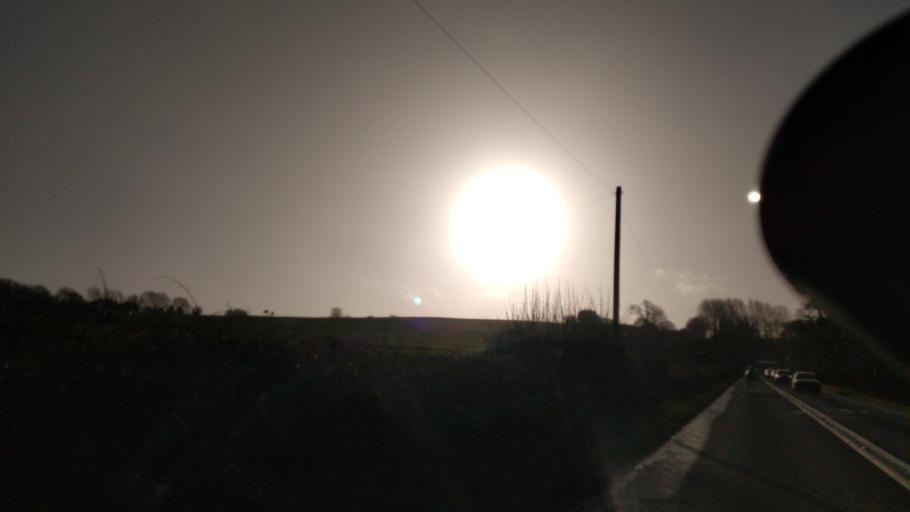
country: GB
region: England
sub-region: Somerset
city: Evercreech
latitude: 51.1432
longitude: -2.5482
